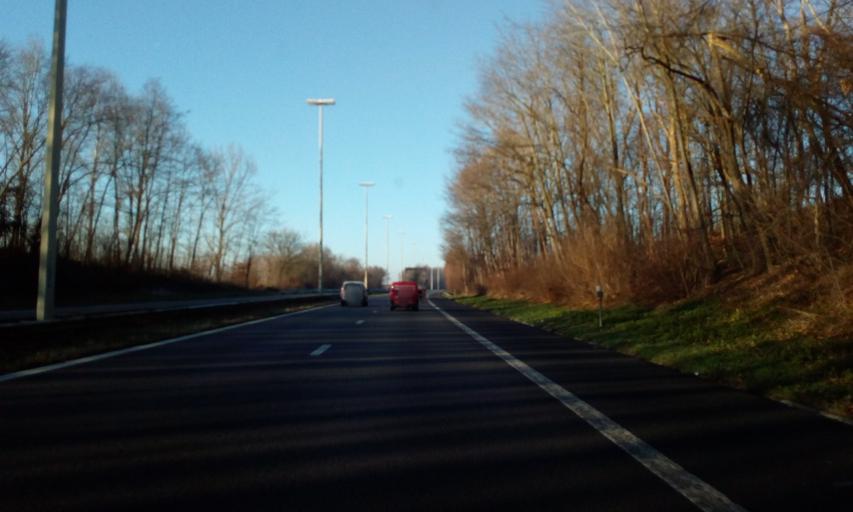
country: BE
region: Wallonia
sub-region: Province du Hainaut
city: Pont-a-Celles
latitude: 50.5257
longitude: 4.3866
